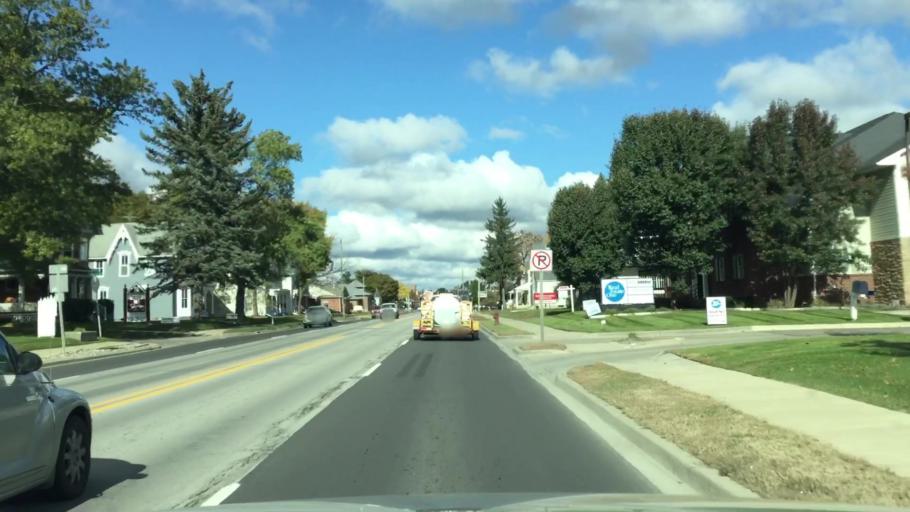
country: US
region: Michigan
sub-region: Oakland County
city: Oxford
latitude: 42.8202
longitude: -83.2608
